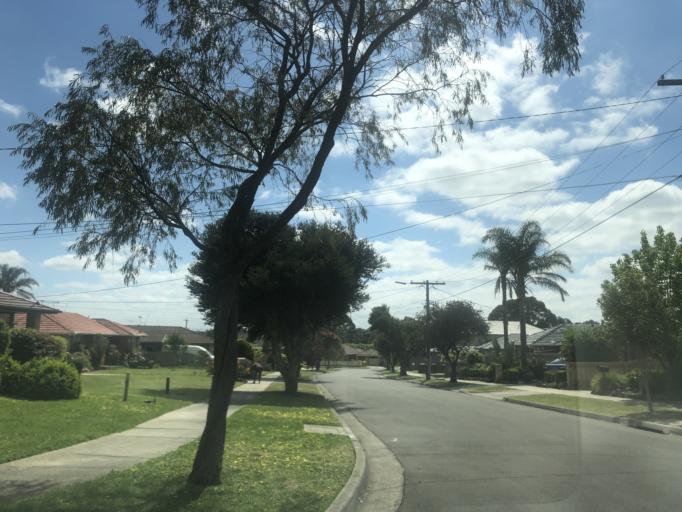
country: AU
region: Victoria
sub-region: Monash
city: Mulgrave
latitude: -37.9220
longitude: 145.1702
